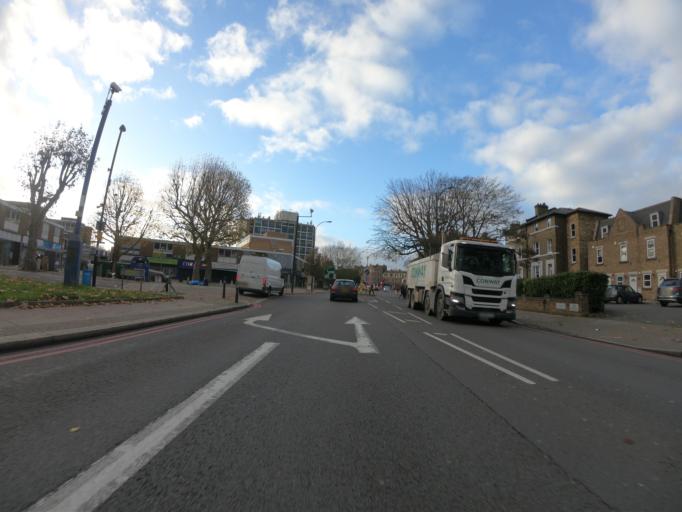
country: GB
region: England
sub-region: Greater London
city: Blackheath
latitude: 51.4559
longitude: 0.0135
